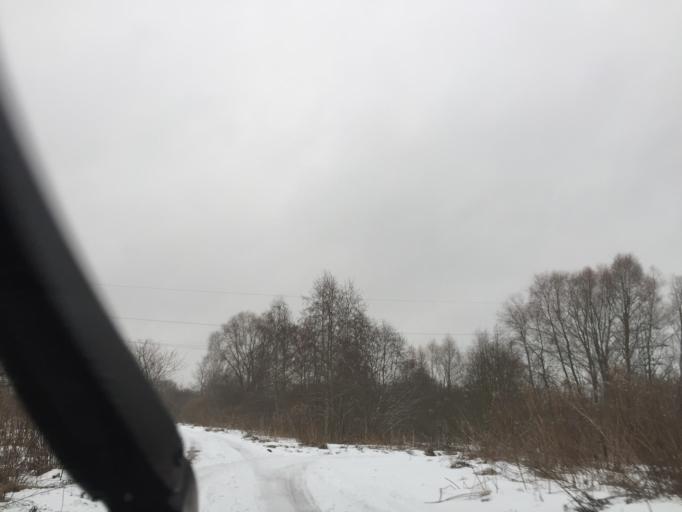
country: LV
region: Riga
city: Riga
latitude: 56.9210
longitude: 24.1328
